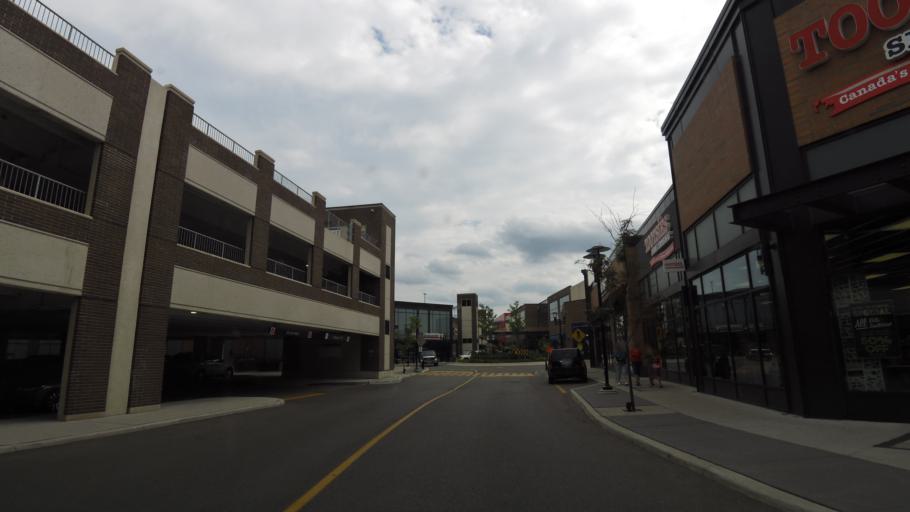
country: CA
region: Ontario
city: Toronto
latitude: 43.6743
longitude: -79.4711
